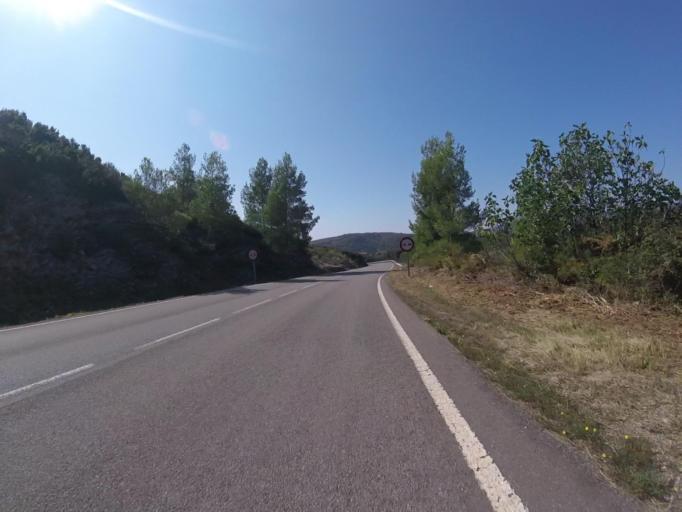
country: ES
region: Valencia
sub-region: Provincia de Castello
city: Benafigos
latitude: 40.2545
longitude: -0.2127
